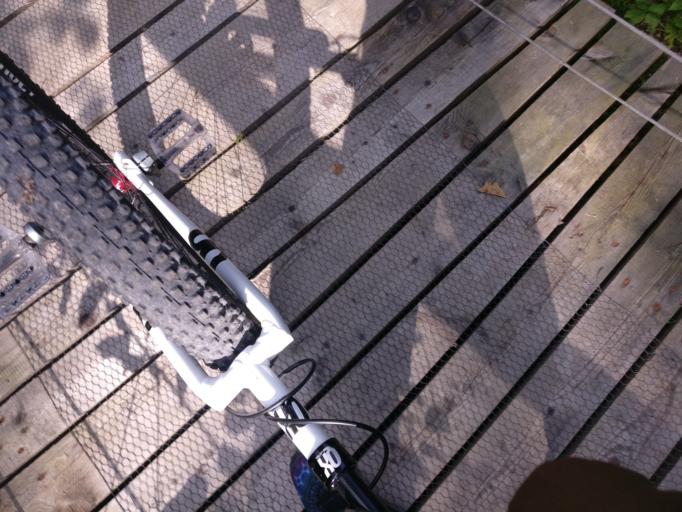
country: AT
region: Styria
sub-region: Politischer Bezirk Liezen
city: Johnsbach
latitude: 47.5828
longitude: 14.5877
